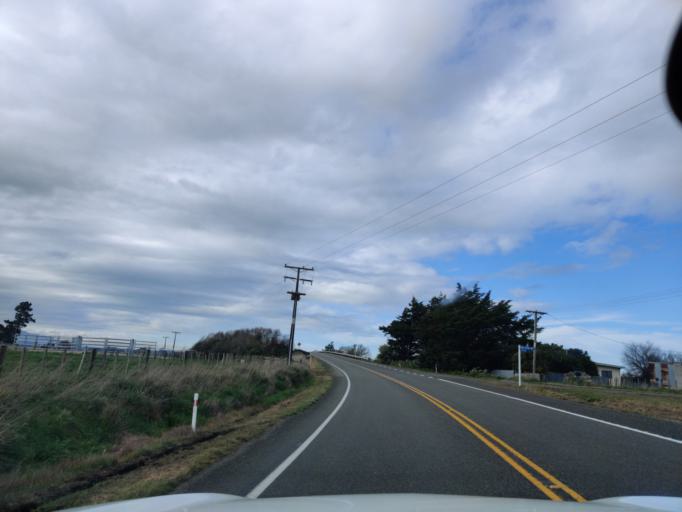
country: NZ
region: Manawatu-Wanganui
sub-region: Palmerston North City
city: Palmerston North
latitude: -40.3360
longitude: 175.8410
